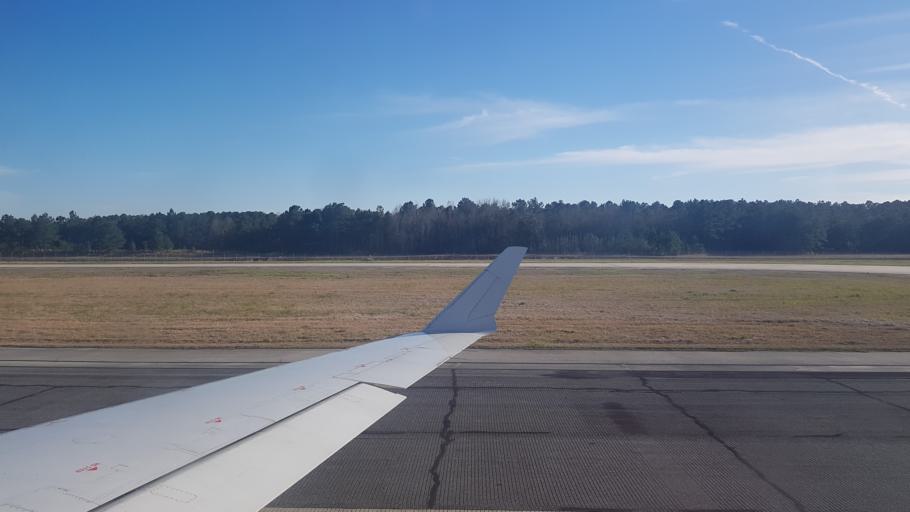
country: US
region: Georgia
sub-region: Chatham County
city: Pooler
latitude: 32.1287
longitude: -81.2181
